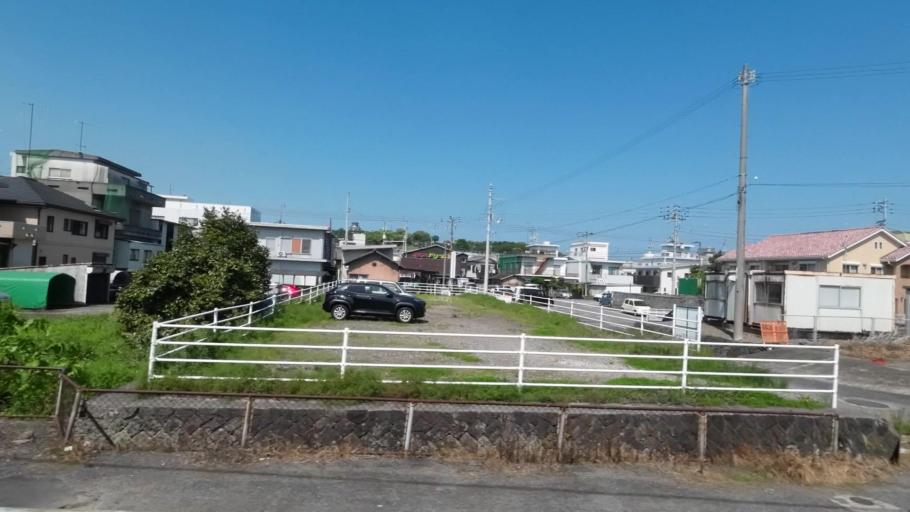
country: JP
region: Ehime
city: Kawanoecho
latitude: 34.0132
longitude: 133.5758
